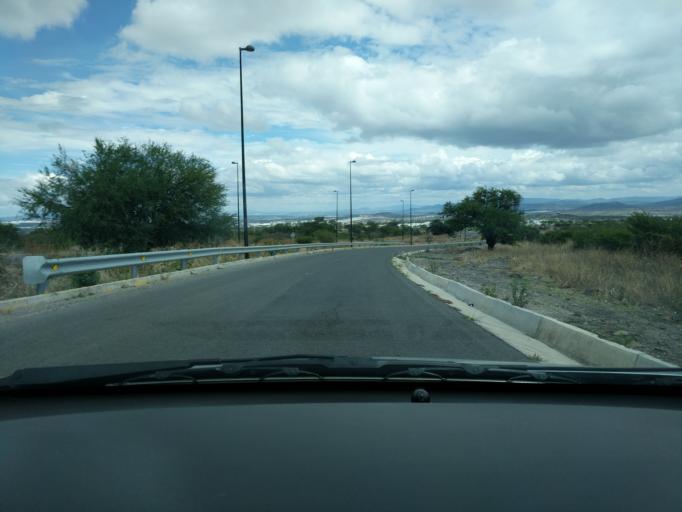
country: MX
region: Queretaro
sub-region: El Marques
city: La Pradera
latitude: 20.6685
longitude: -100.3167
